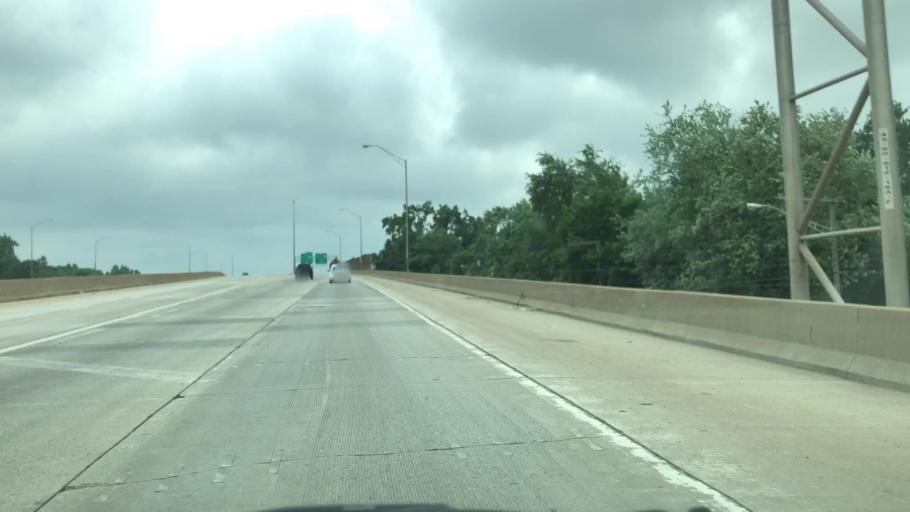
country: US
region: Indiana
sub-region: Lake County
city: Highland
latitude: 41.5773
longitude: -87.4330
